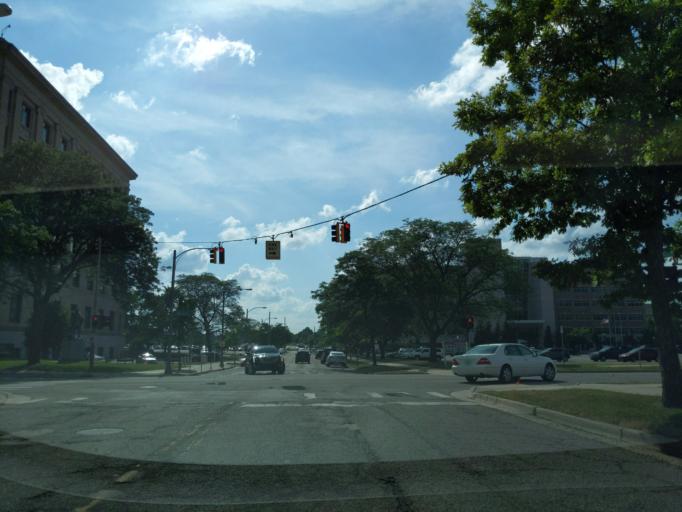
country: US
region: Michigan
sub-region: Ingham County
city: Lansing
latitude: 42.7313
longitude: -84.5567
